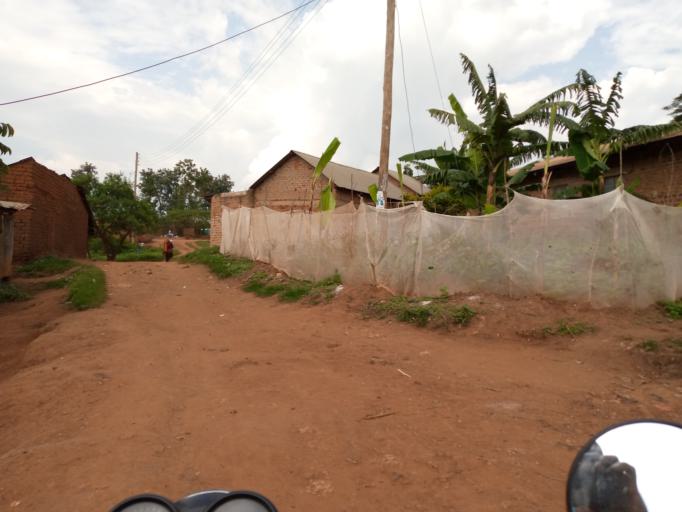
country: UG
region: Eastern Region
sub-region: Mbale District
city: Mbale
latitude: 1.0817
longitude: 34.1656
